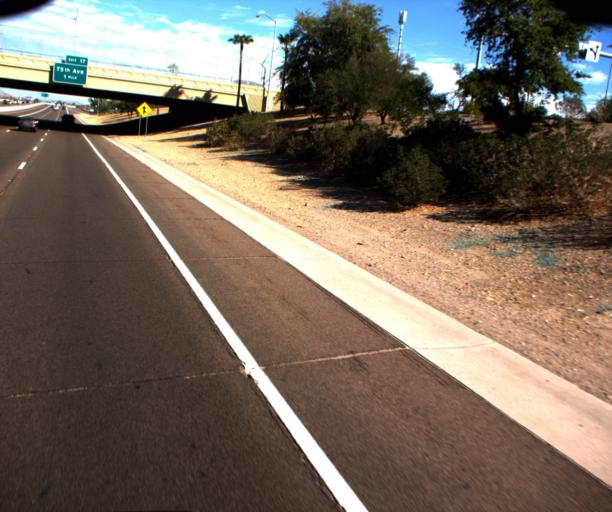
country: US
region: Arizona
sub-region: Maricopa County
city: Sun City
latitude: 33.6518
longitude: -112.2322
